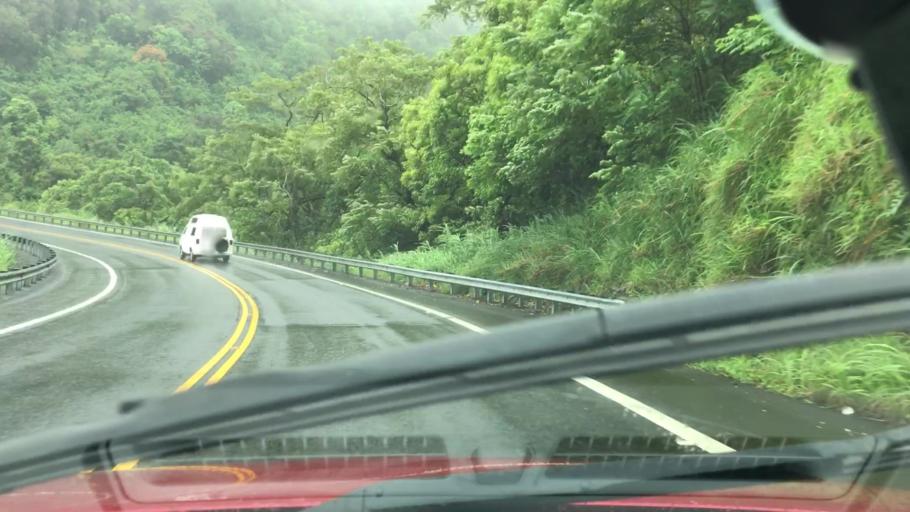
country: US
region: Hawaii
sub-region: Hawaii County
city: Pepeekeo
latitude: 19.9876
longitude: -155.2494
